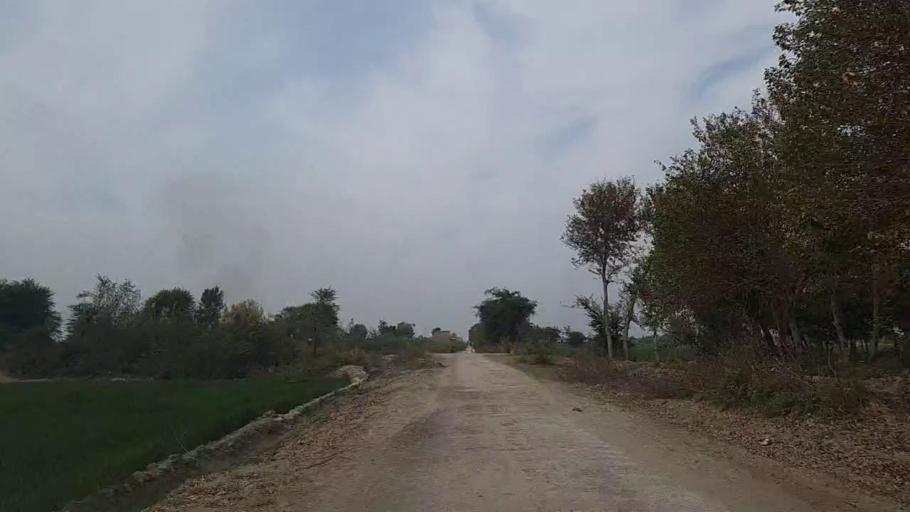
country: PK
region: Sindh
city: Daur
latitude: 26.4461
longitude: 68.4535
